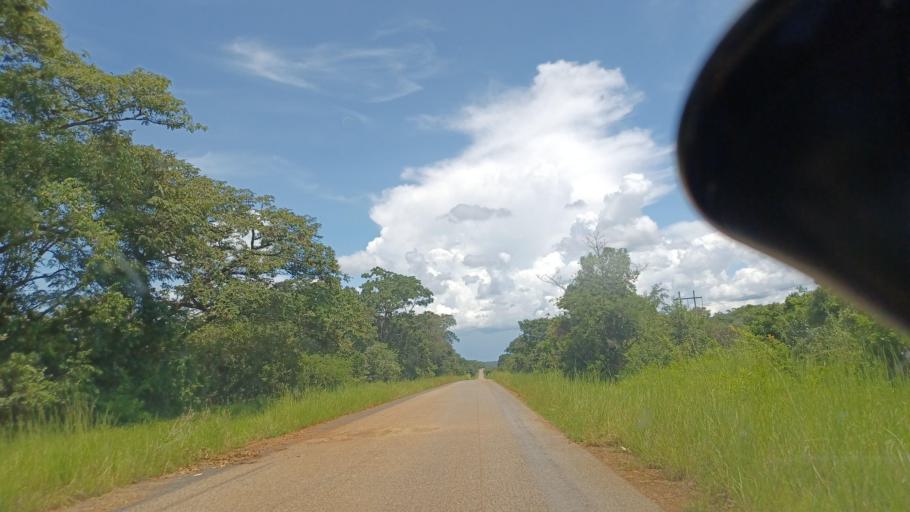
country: ZM
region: North-Western
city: Solwezi
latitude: -12.5934
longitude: 26.1277
